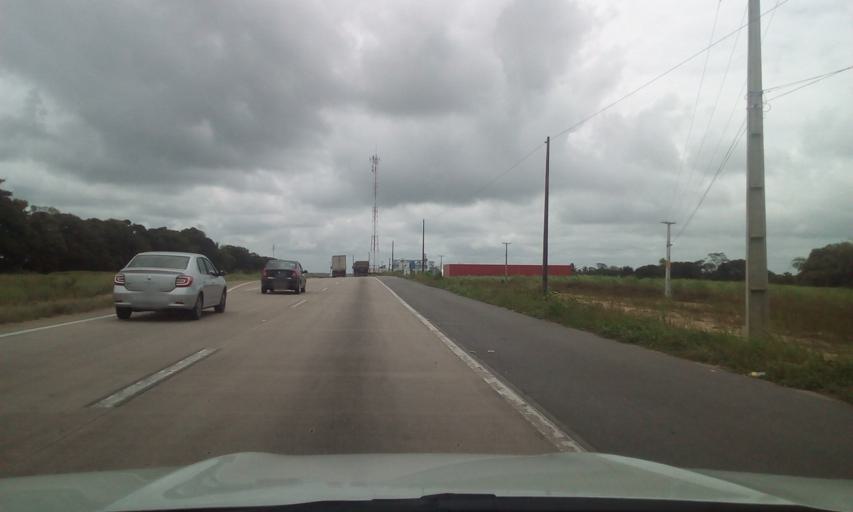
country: BR
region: Pernambuco
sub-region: Itapissuma
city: Itapissuma
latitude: -7.7966
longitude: -34.9268
